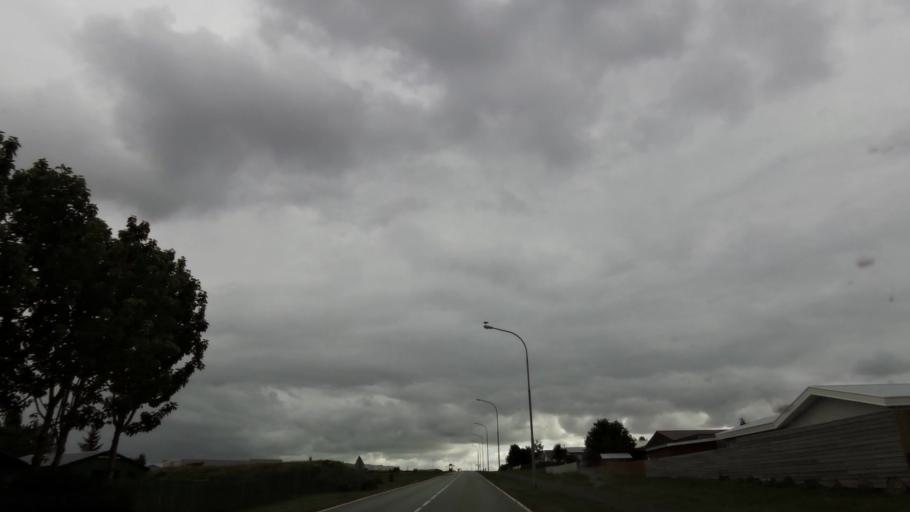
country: IS
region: Capital Region
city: Alftanes
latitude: 64.1041
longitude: -22.0272
